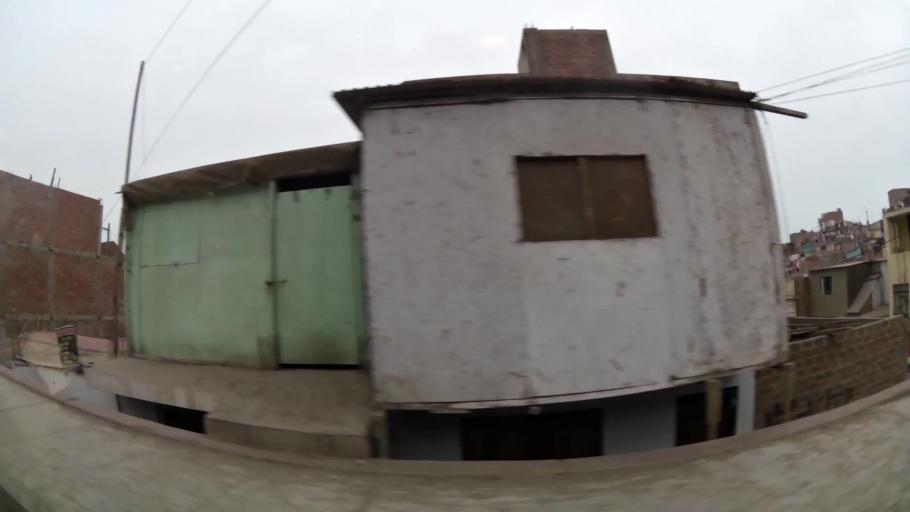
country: PE
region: Lima
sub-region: Lima
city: Surco
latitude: -12.1951
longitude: -77.0279
